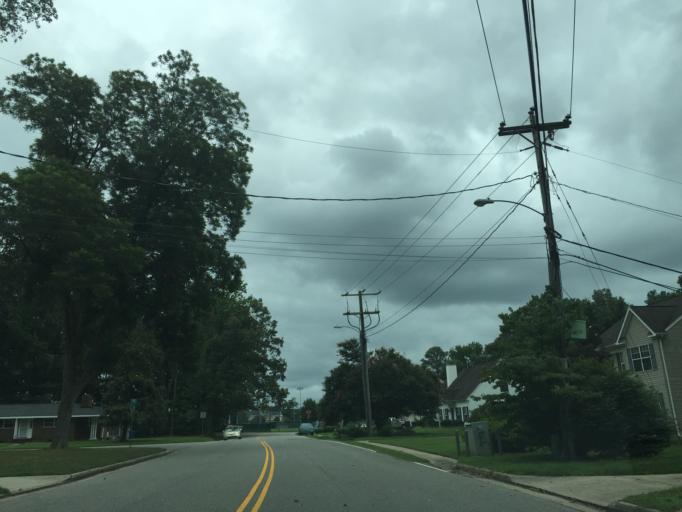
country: US
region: Virginia
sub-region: City of Newport News
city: Newport News
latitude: 37.0654
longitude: -76.5032
